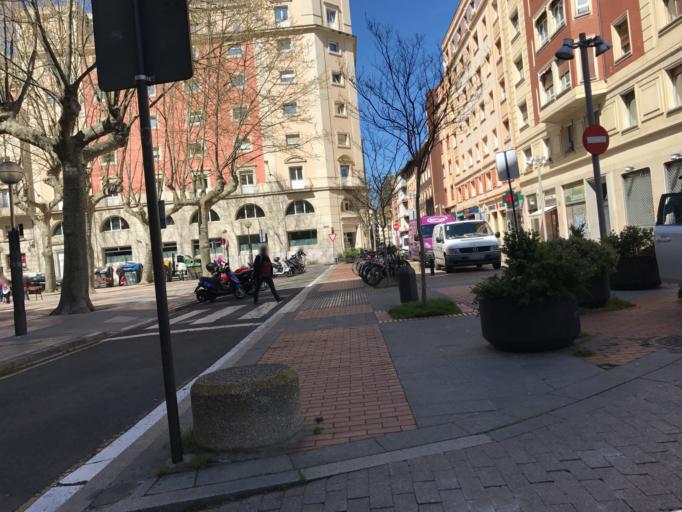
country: ES
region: Basque Country
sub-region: Provincia de Alava
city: Gasteiz / Vitoria
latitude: 42.8473
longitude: -2.6763
